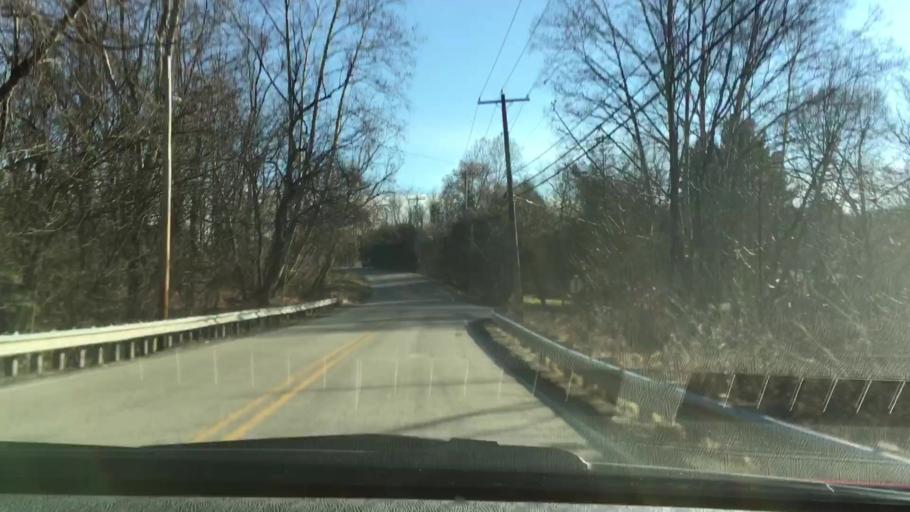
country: US
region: Pennsylvania
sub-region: Westmoreland County
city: Irwin
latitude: 40.2650
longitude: -79.6982
